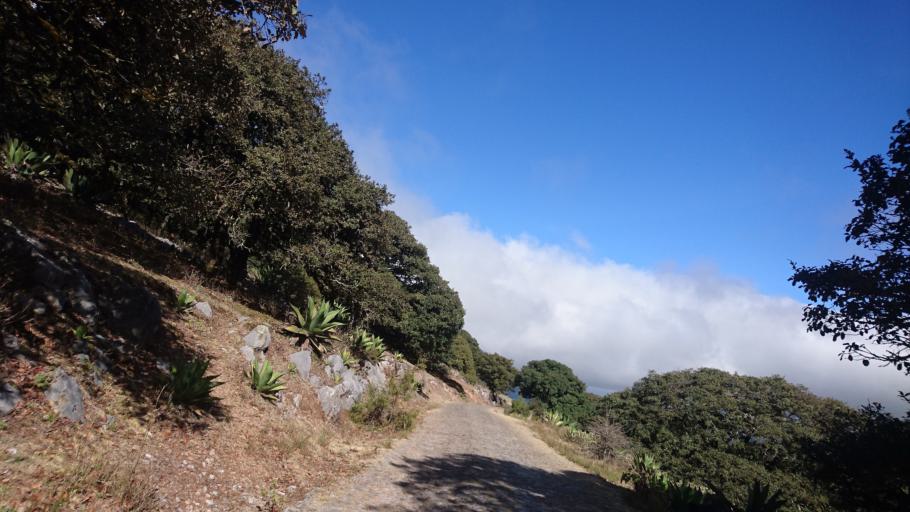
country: MX
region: San Luis Potosi
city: Zaragoza
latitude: 22.0653
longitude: -100.6420
